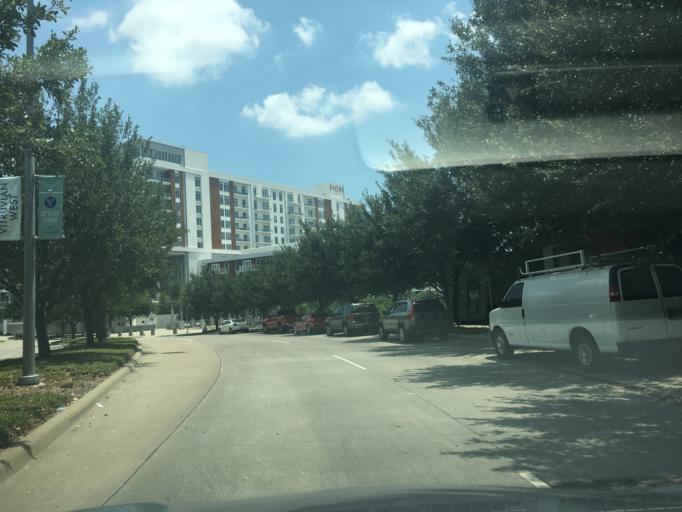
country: US
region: Texas
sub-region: Dallas County
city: Addison
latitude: 32.9365
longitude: -96.8506
